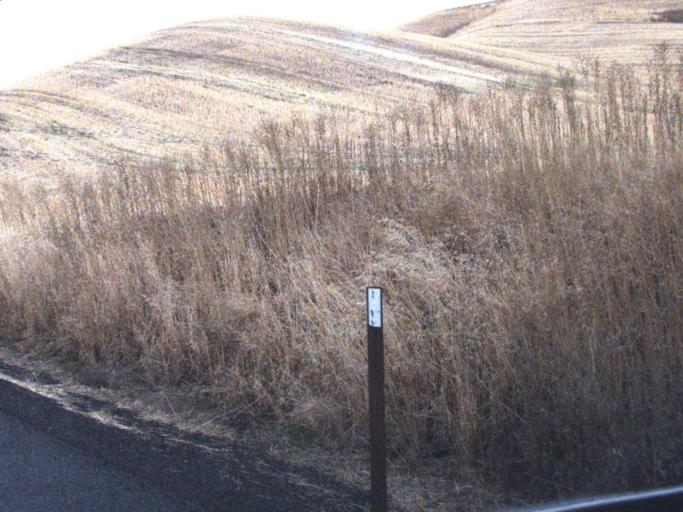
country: US
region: Washington
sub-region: Whitman County
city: Colfax
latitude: 46.8580
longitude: -117.4590
